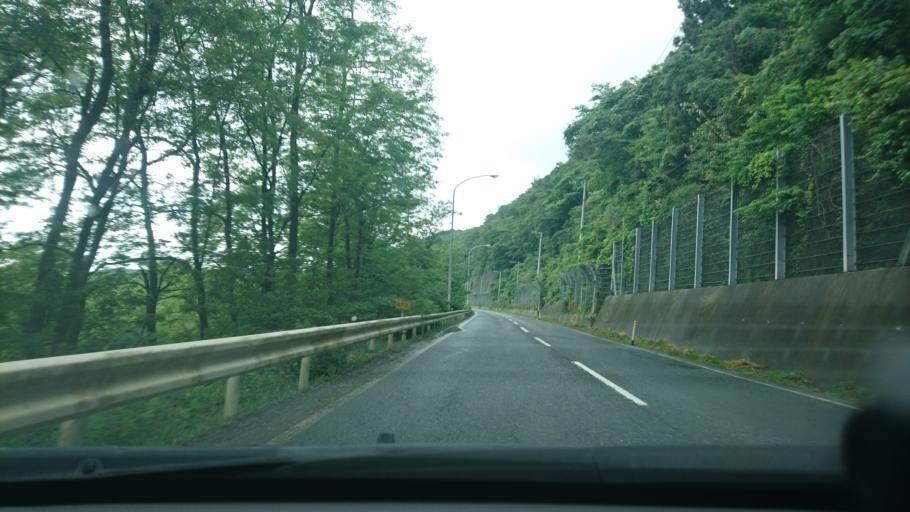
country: JP
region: Miyagi
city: Ishinomaki
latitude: 38.5569
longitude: 141.3067
